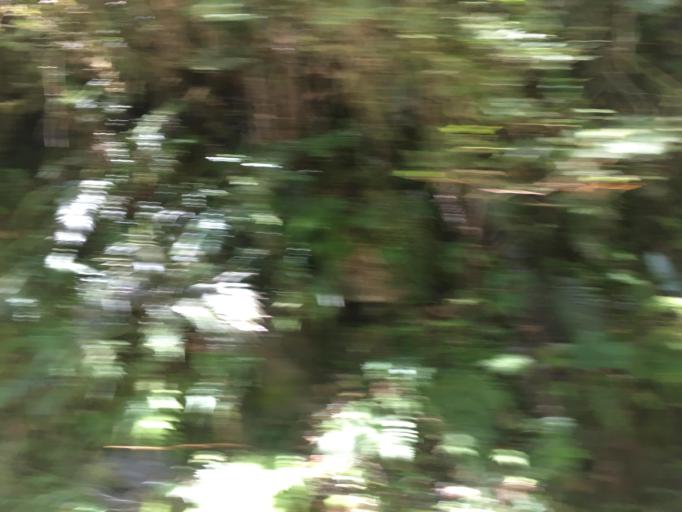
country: TW
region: Taiwan
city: Daxi
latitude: 24.5853
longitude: 121.4120
